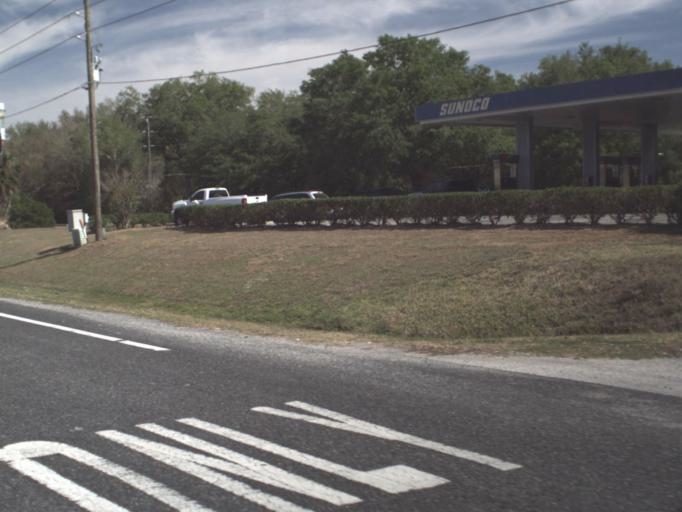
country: US
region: Florida
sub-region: Lake County
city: Lady Lake
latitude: 28.9079
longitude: -81.9170
